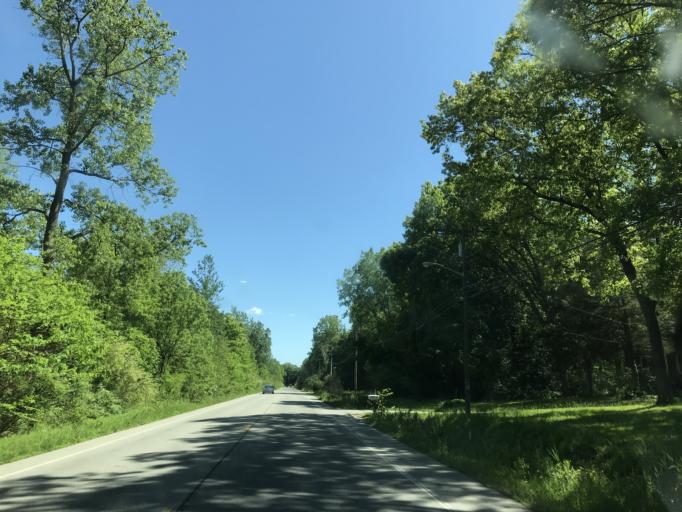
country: US
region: Michigan
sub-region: Wayne County
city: Woodhaven
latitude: 42.1728
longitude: -83.2864
